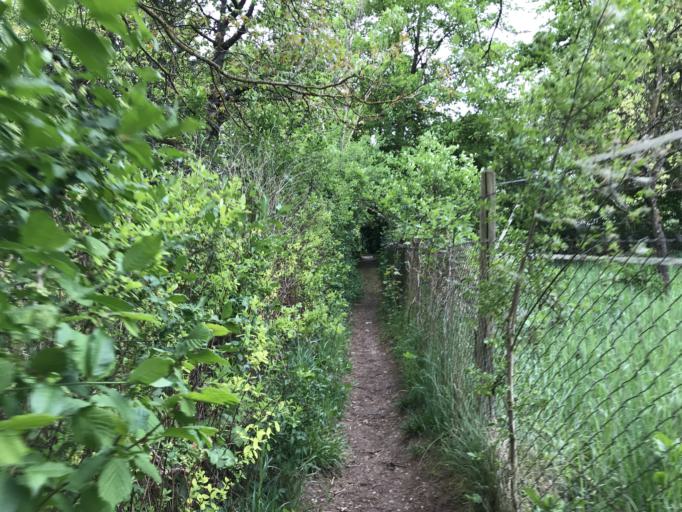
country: DE
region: Baden-Wuerttemberg
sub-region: Regierungsbezirk Stuttgart
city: Leinfelden-Echterdingen
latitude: 48.7423
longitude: 9.1166
